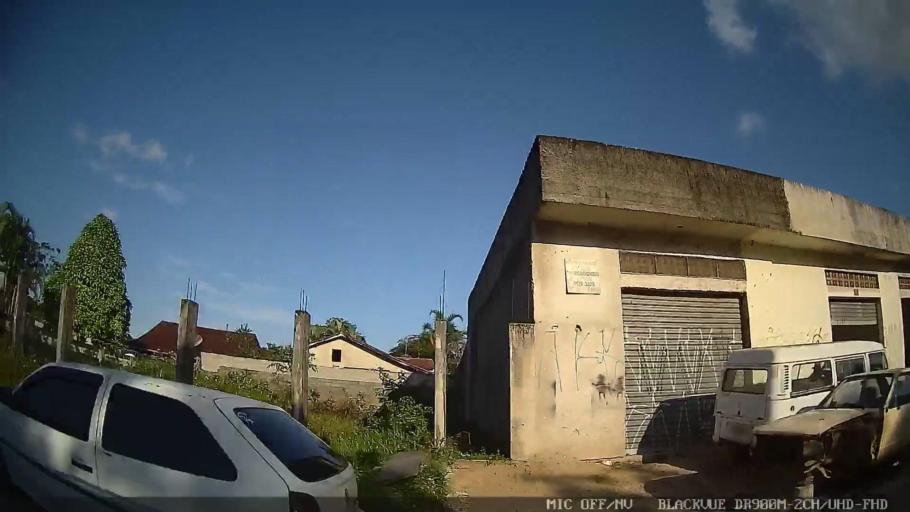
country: BR
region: Sao Paulo
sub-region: Itanhaem
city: Itanhaem
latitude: -24.1604
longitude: -46.8317
